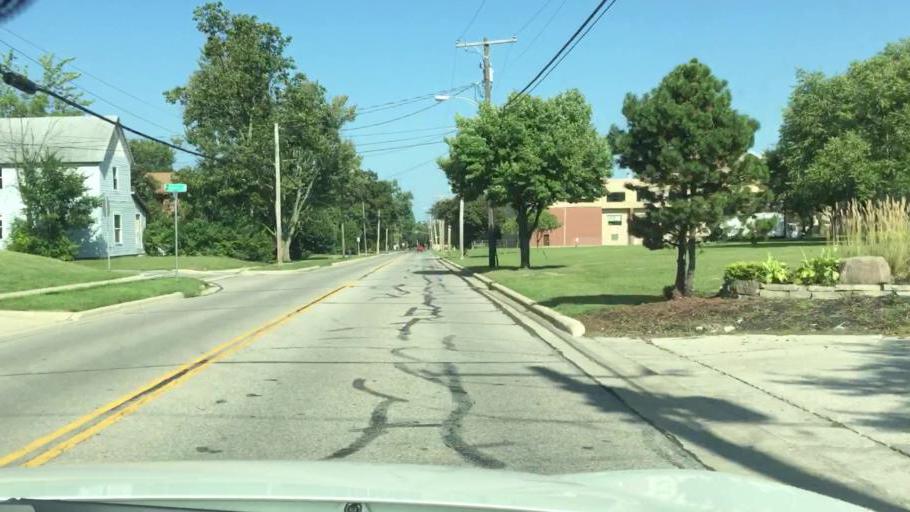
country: US
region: Ohio
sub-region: Union County
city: Marysville
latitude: 40.2302
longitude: -83.3783
